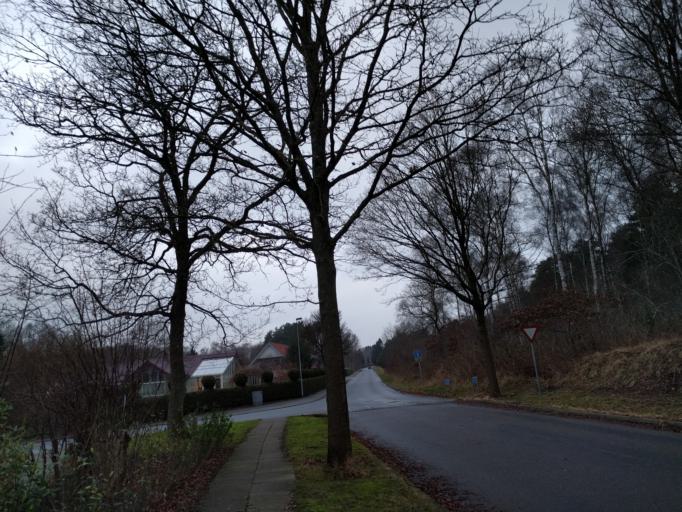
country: DK
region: Central Jutland
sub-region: Silkeborg Kommune
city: Silkeborg
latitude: 56.1862
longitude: 9.5338
